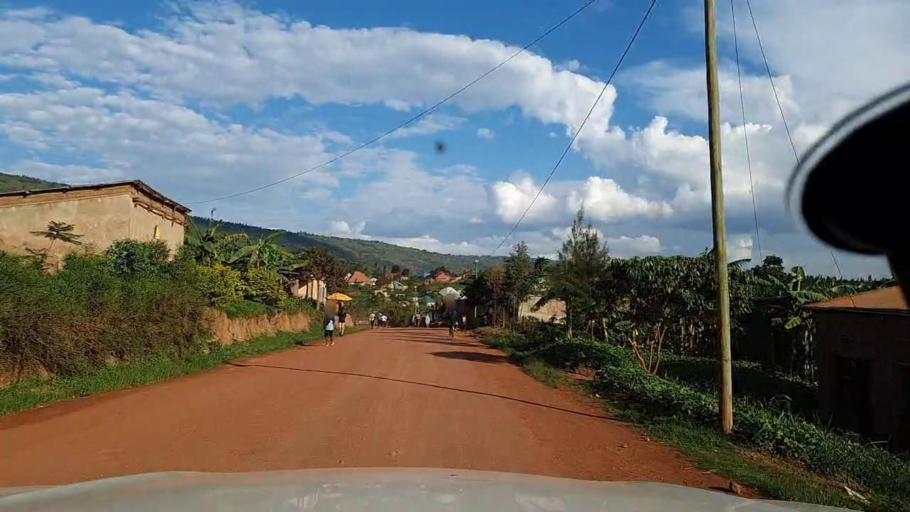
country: RW
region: Kigali
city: Kigali
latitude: -1.8938
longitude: 29.9614
